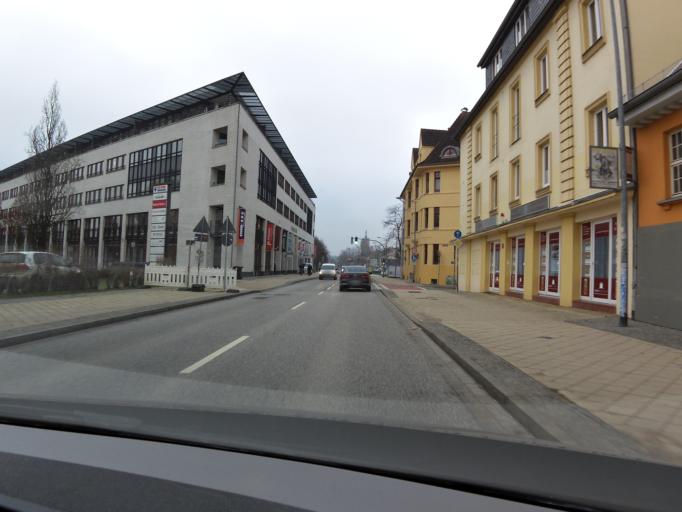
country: DE
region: Mecklenburg-Vorpommern
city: Schelfstadt
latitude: 53.6315
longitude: 11.4215
